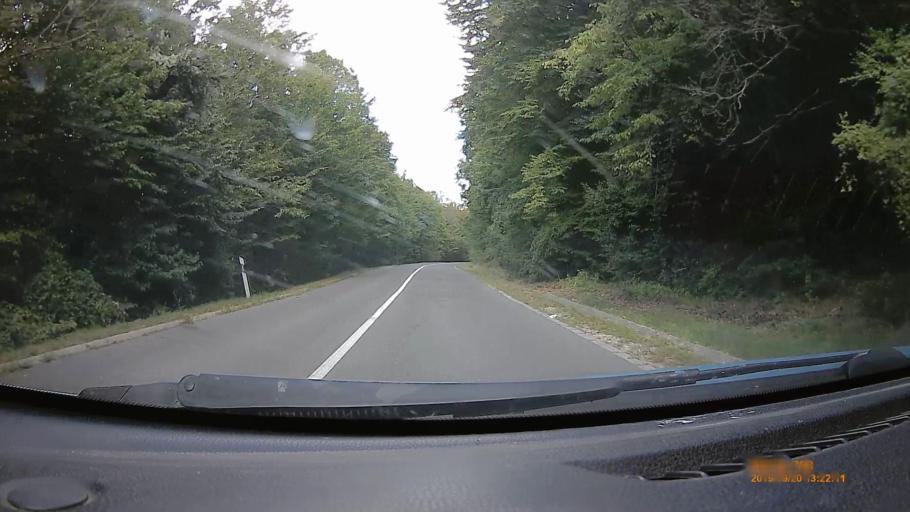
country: HU
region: Heves
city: Felsotarkany
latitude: 48.0267
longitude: 20.4753
